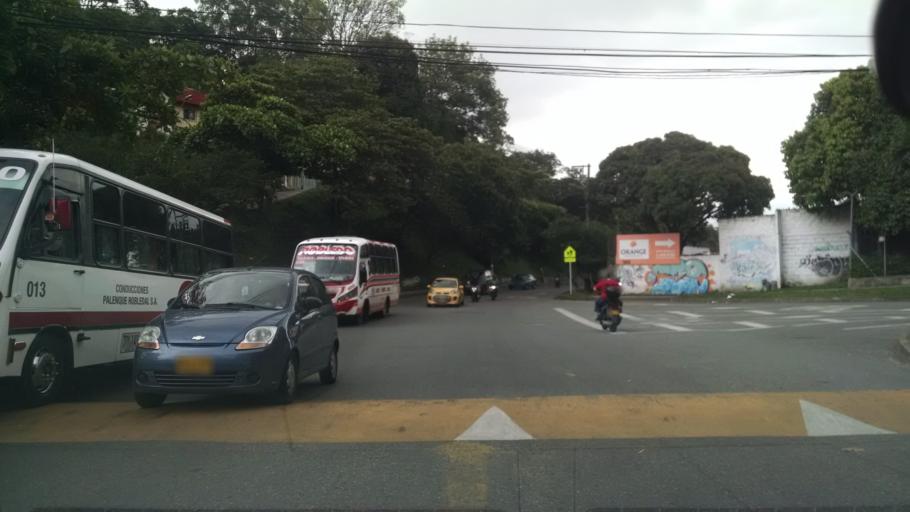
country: CO
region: Antioquia
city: Medellin
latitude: 6.2703
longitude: -75.5877
